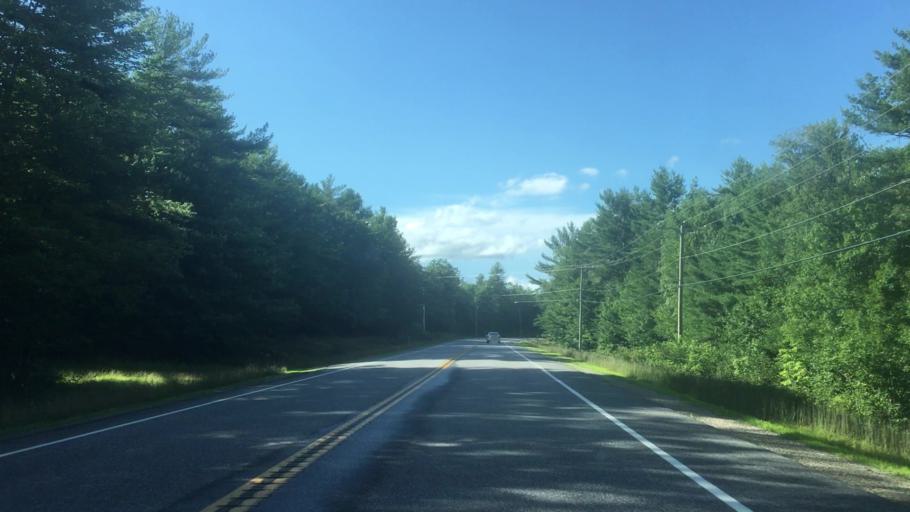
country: US
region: New Hampshire
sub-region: Cheshire County
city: Harrisville
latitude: 43.0456
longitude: -72.0756
